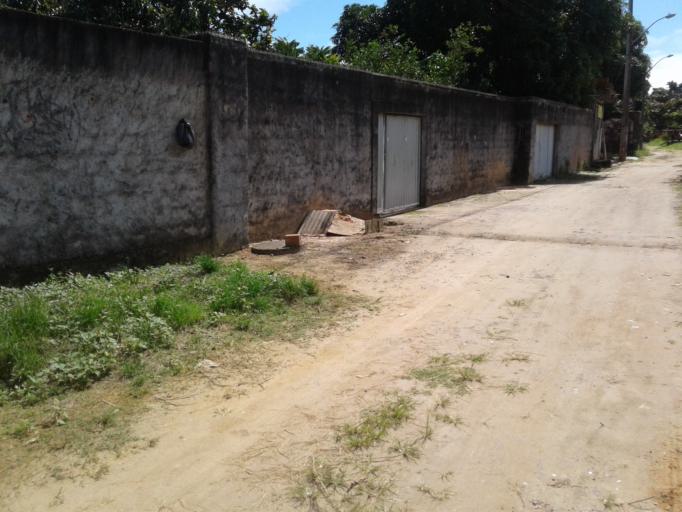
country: BR
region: Bahia
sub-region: Salvador
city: Salvador
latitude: -12.8825
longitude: -38.4744
